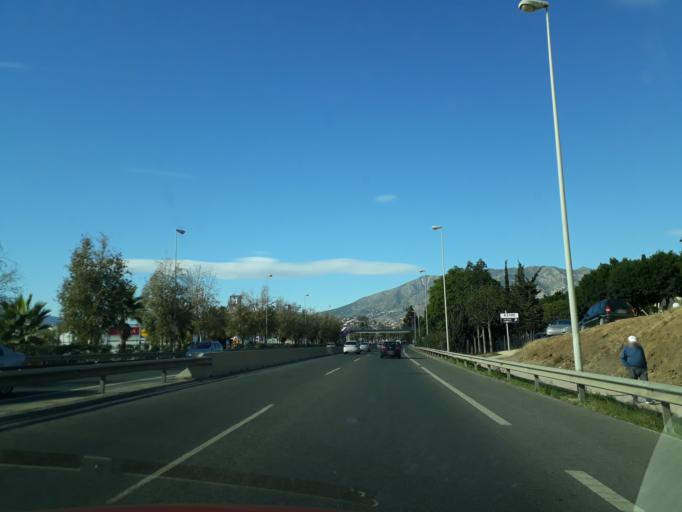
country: ES
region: Andalusia
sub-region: Provincia de Malaga
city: Fuengirola
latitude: 36.5344
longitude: -4.6326
